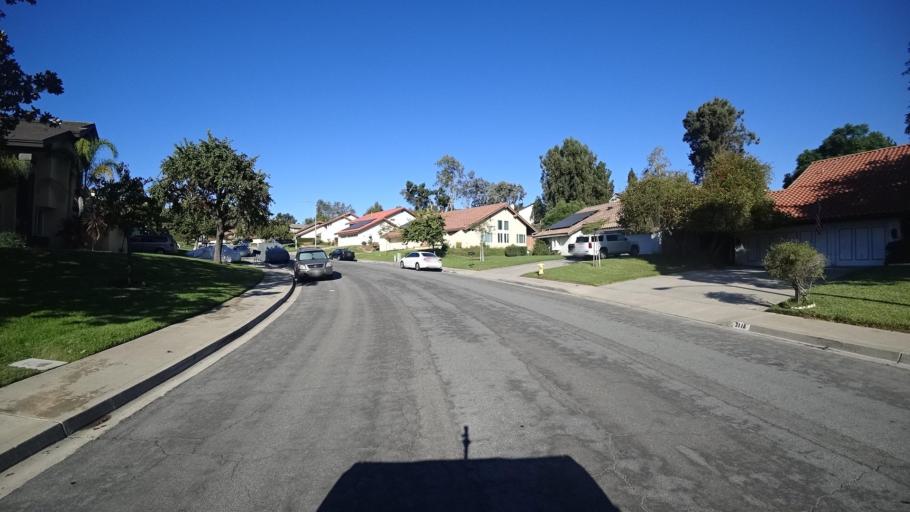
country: US
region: California
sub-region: San Diego County
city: Bonita
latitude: 32.6778
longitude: -117.0276
